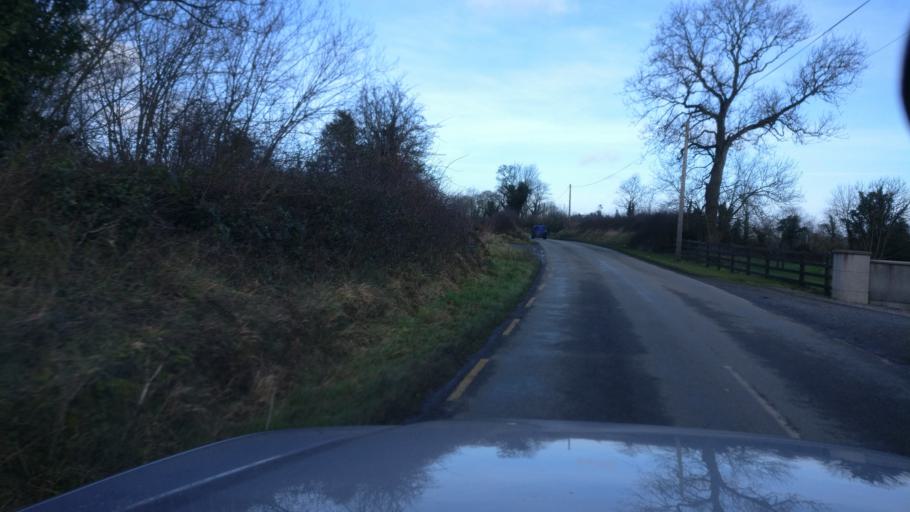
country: IE
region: Leinster
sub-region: Kilkenny
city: Castlecomer
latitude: 52.8339
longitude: -7.1950
